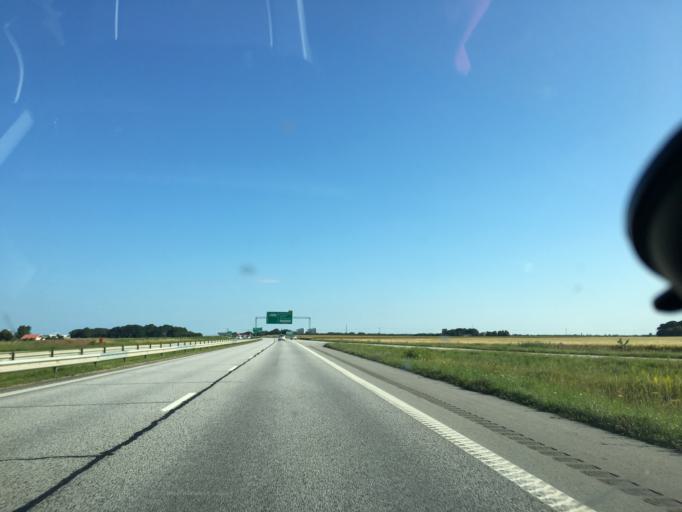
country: SE
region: Skane
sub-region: Malmo
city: Tygelsjo
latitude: 55.5328
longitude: 13.0072
